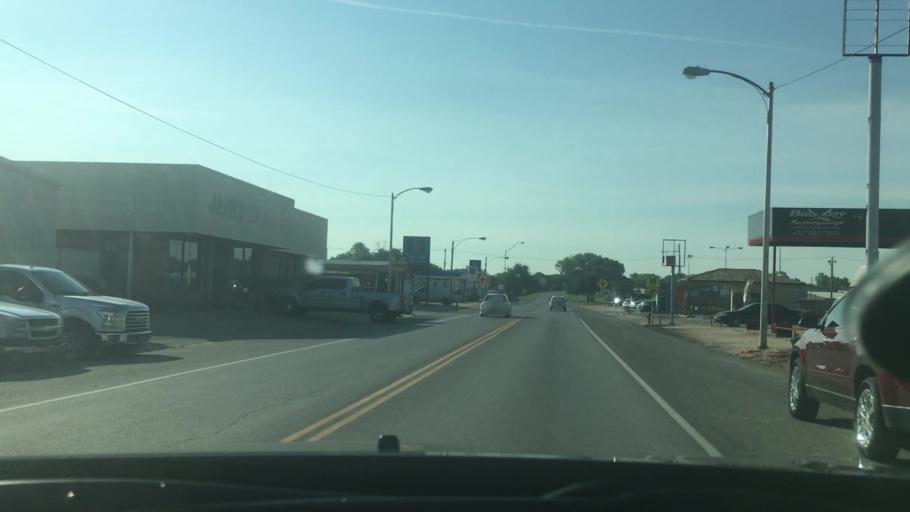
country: US
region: Oklahoma
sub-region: Garvin County
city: Pauls Valley
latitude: 34.7387
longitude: -97.2176
